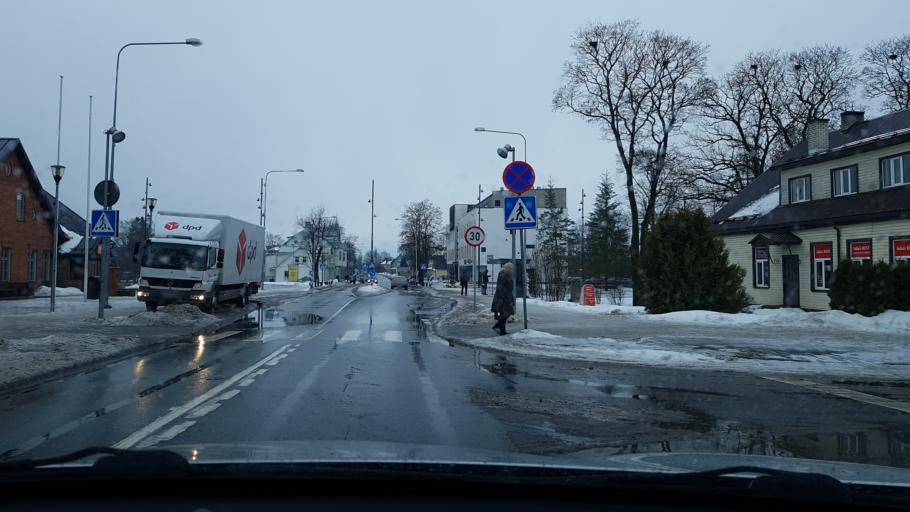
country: EE
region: Raplamaa
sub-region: Rapla vald
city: Rapla
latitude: 59.0049
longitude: 24.7937
